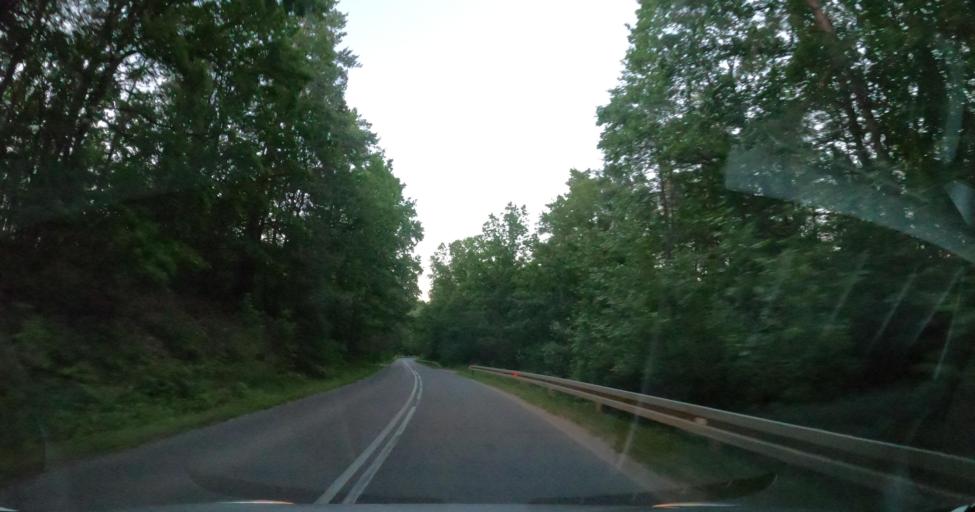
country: PL
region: Pomeranian Voivodeship
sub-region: Powiat wejherowski
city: Linia
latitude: 54.4592
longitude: 17.9545
